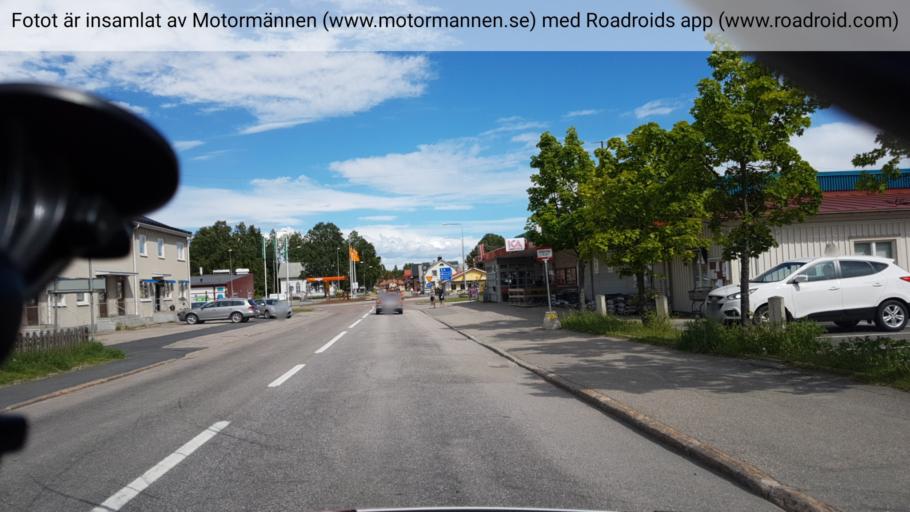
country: SE
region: Gaevleborg
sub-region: Bollnas Kommun
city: Kilafors
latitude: 61.2297
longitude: 16.5615
